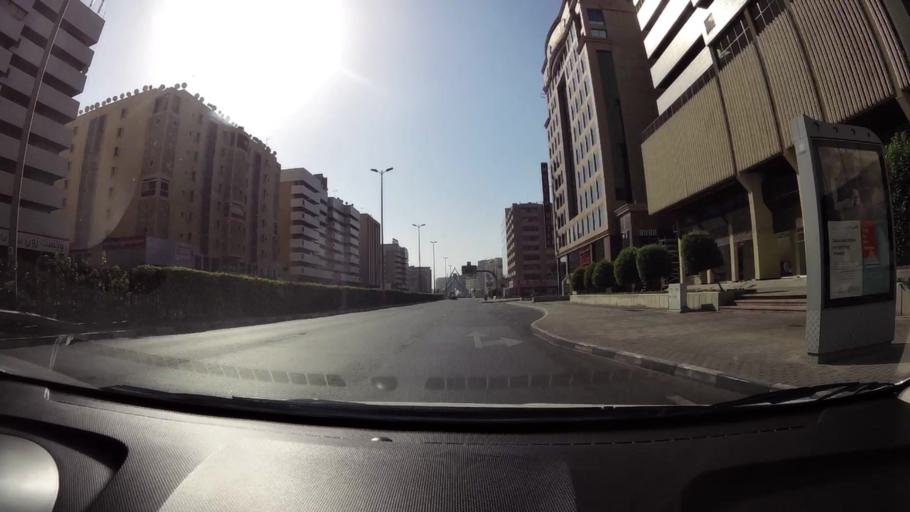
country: AE
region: Ash Shariqah
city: Sharjah
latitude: 25.2598
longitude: 55.3224
